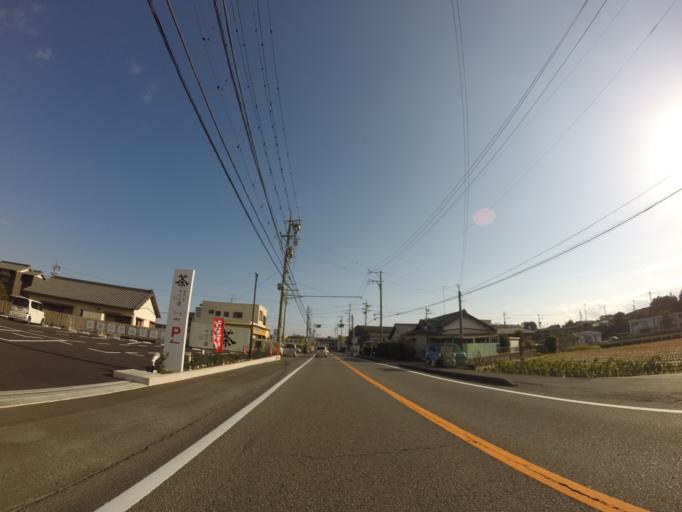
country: JP
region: Shizuoka
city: Shimada
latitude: 34.8134
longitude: 138.2159
